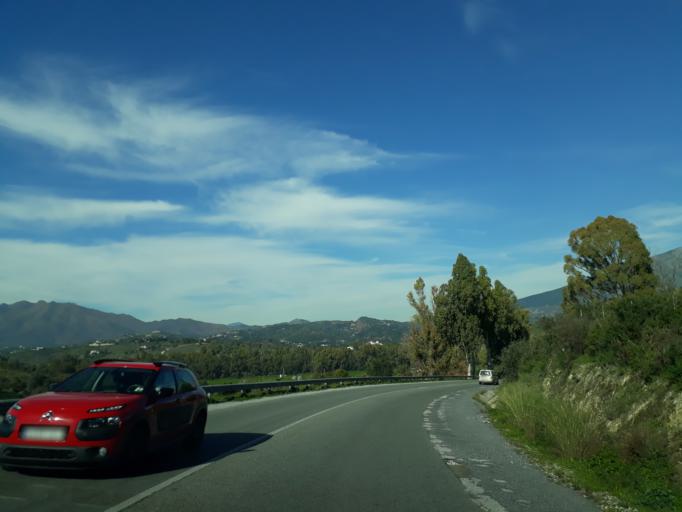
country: ES
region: Andalusia
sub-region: Provincia de Malaga
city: Fuengirola
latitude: 36.5381
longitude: -4.6876
